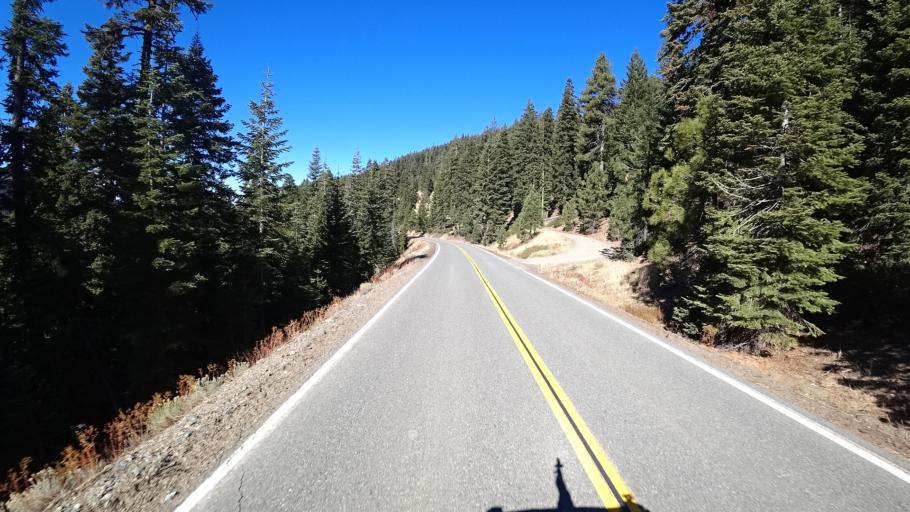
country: US
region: California
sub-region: Trinity County
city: Weaverville
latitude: 41.2207
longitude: -122.8997
